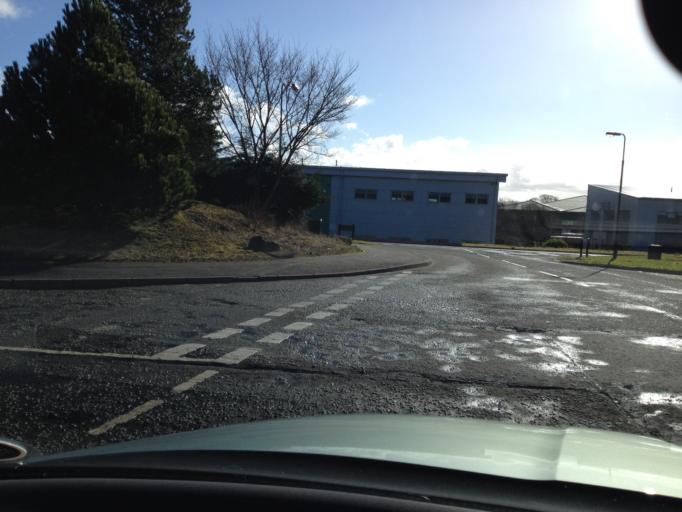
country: GB
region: Scotland
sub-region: West Lothian
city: Livingston
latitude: 55.8908
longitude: -3.5305
